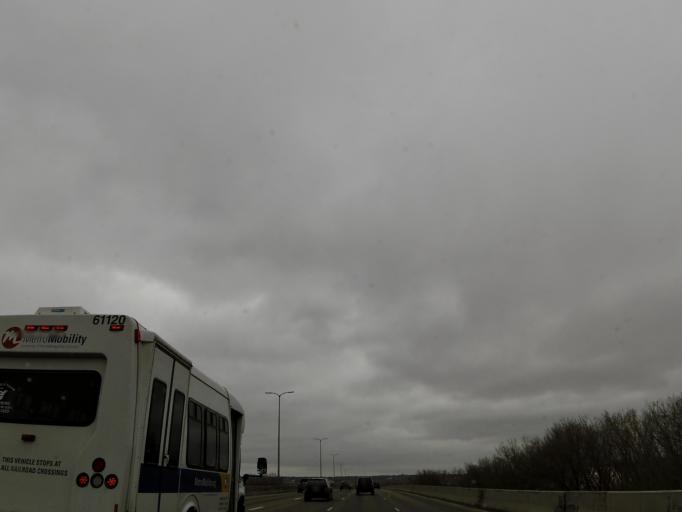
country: US
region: Minnesota
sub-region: Dakota County
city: Burnsville
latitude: 44.8029
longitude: -93.2906
